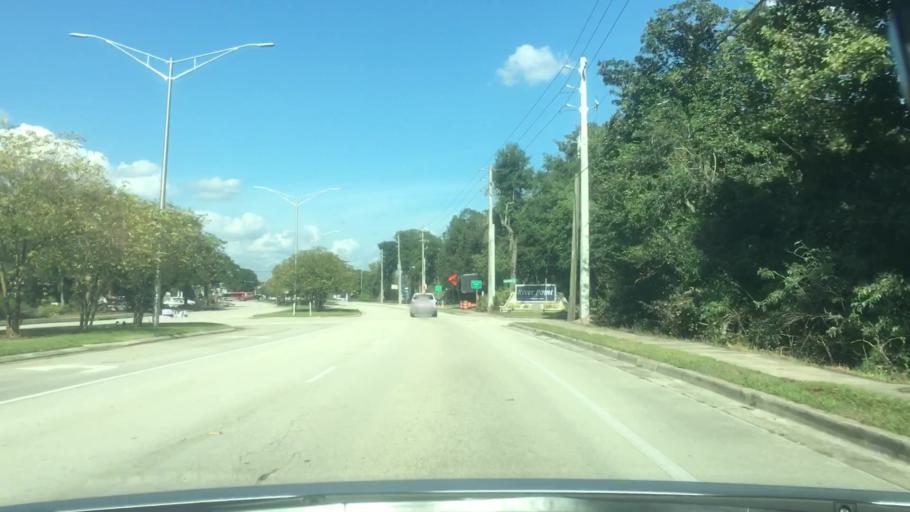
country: US
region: Florida
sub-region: Duval County
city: Atlantic Beach
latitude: 30.3575
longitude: -81.5036
